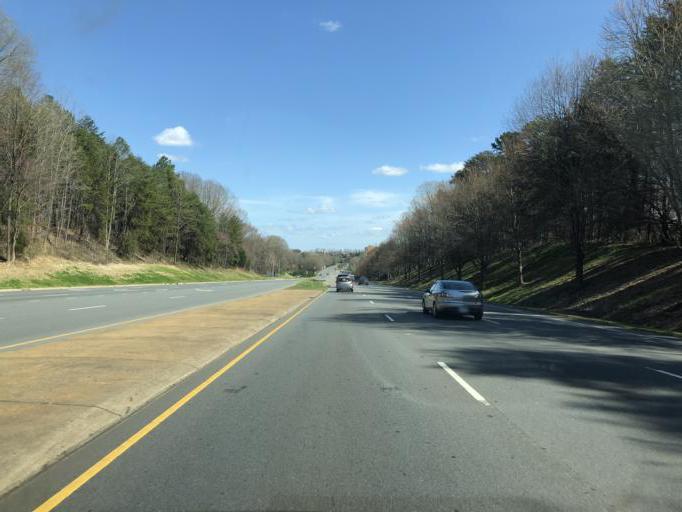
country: US
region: North Carolina
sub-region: Cabarrus County
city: Harrisburg
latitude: 35.3159
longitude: -80.7706
